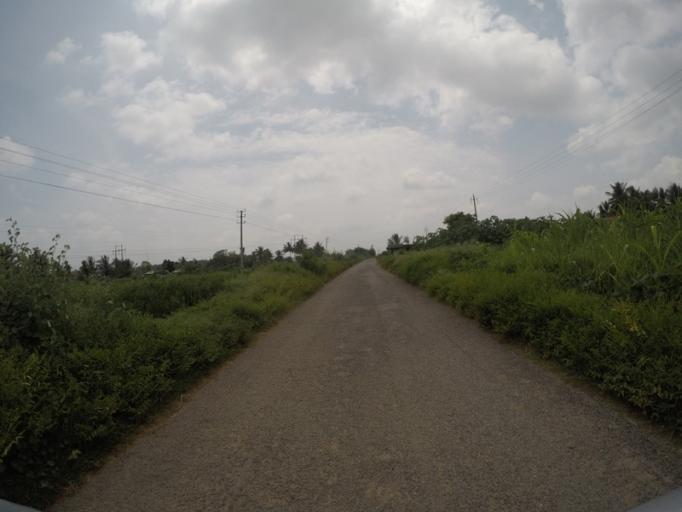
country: IN
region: Karnataka
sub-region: Ramanagara
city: Kanakapura
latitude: 12.6495
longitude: 77.4414
